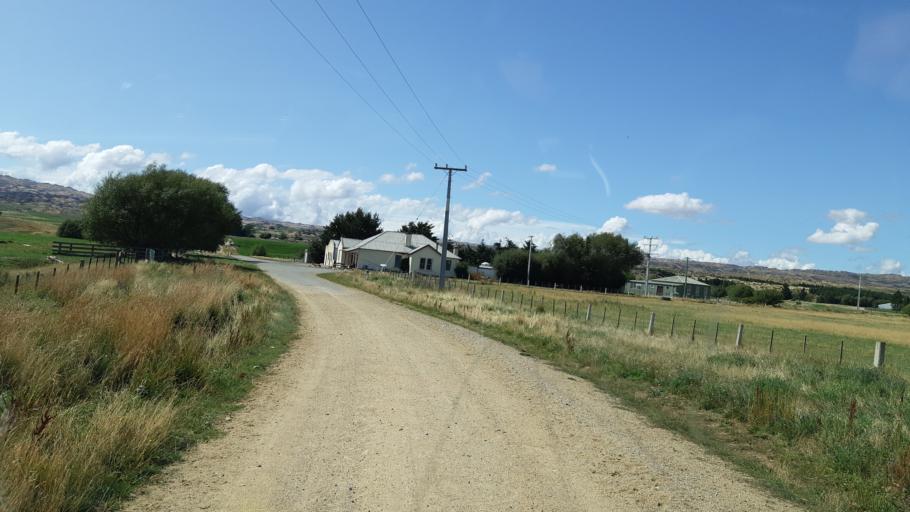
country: NZ
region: Otago
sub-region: Queenstown-Lakes District
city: Wanaka
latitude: -45.2133
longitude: 169.6839
